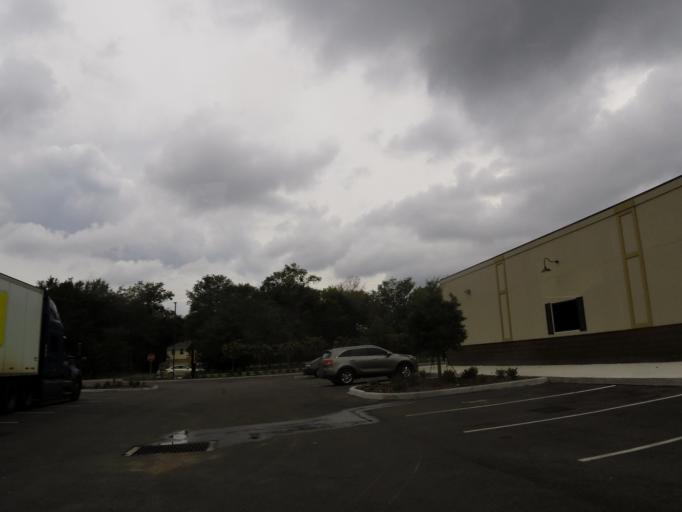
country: US
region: Florida
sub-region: Clay County
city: Middleburg
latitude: 30.1124
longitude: -81.8640
